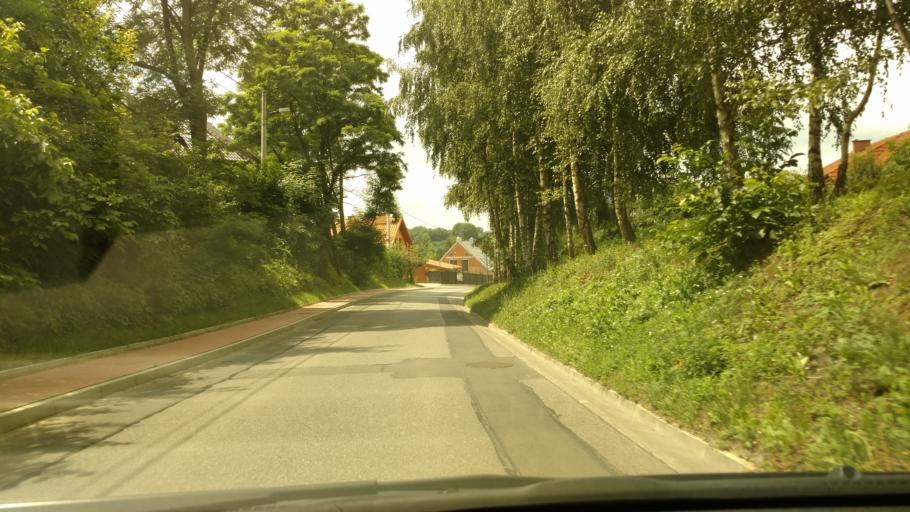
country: PL
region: Lesser Poland Voivodeship
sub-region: Powiat krakowski
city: Zielonki
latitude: 50.1295
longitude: 19.9572
